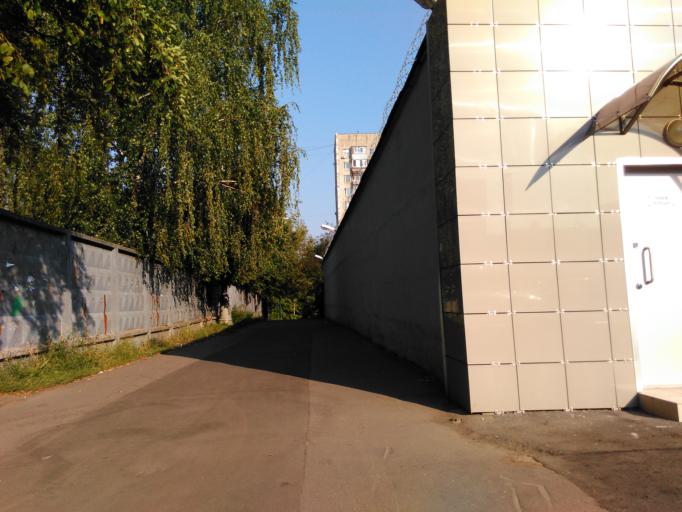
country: RU
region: Moscow
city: Zyuzino
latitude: 55.6421
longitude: 37.5440
